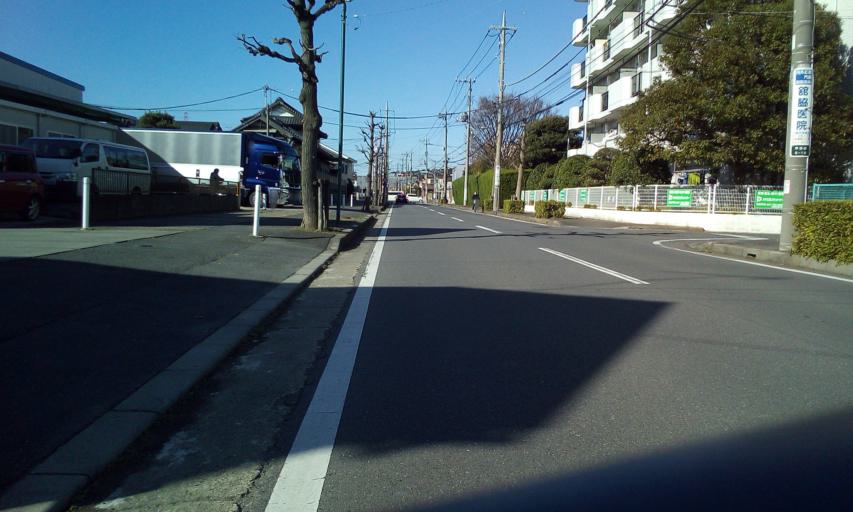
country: JP
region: Chiba
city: Nagareyama
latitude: 35.8559
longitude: 139.8823
